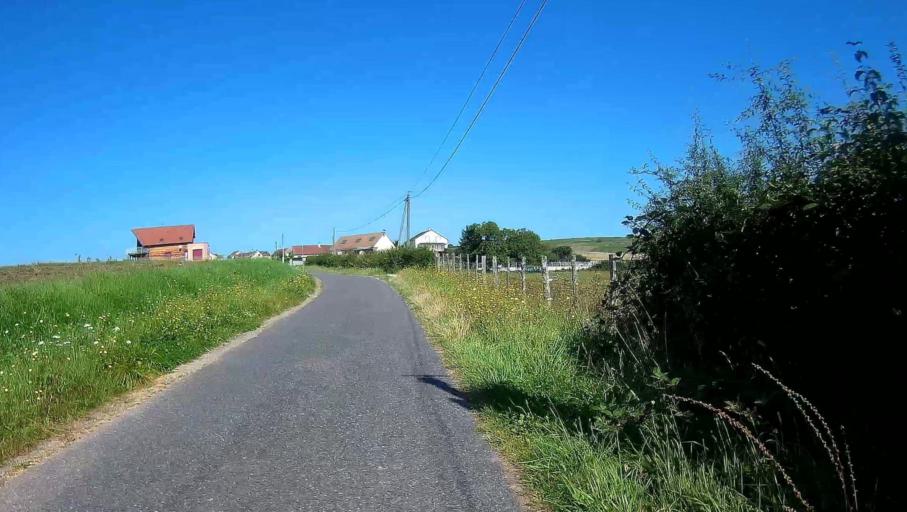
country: FR
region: Bourgogne
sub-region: Departement de Saone-et-Loire
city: Couches
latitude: 46.8402
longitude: 4.5817
